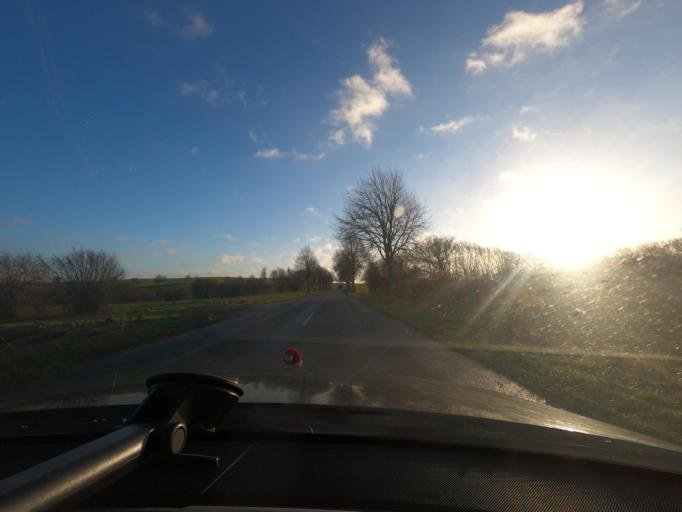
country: DK
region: South Denmark
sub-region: Sonderborg Kommune
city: Broager
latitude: 54.8931
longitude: 9.6847
